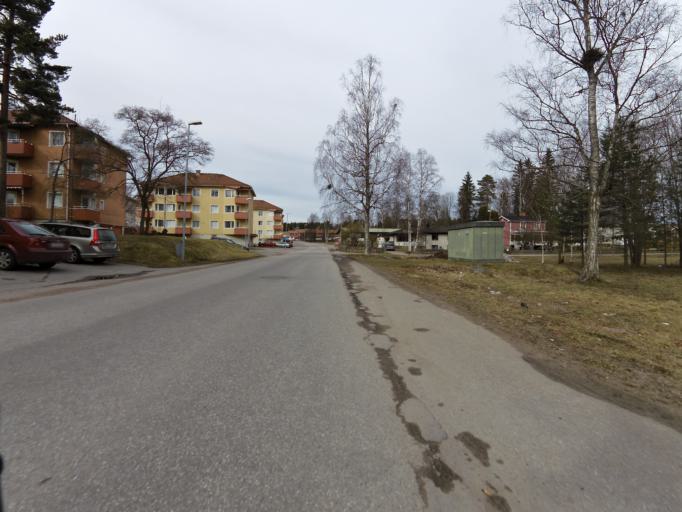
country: SE
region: Gaevleborg
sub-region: Hofors Kommun
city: Hofors
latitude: 60.5431
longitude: 16.2766
